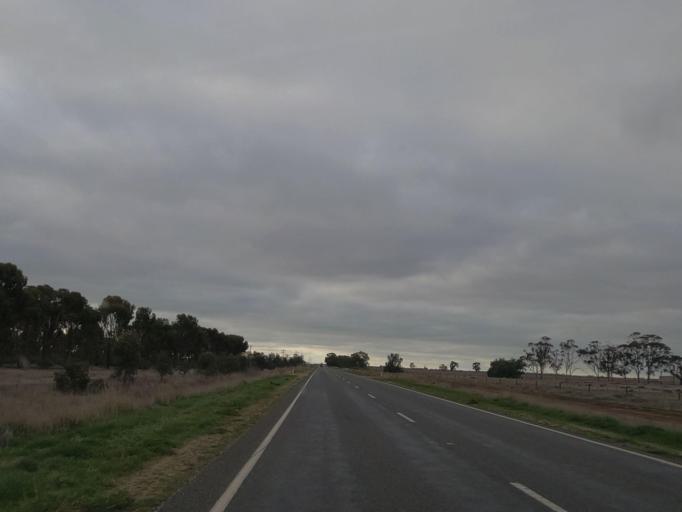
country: AU
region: Victoria
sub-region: Swan Hill
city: Swan Hill
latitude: -35.9182
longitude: 143.9425
